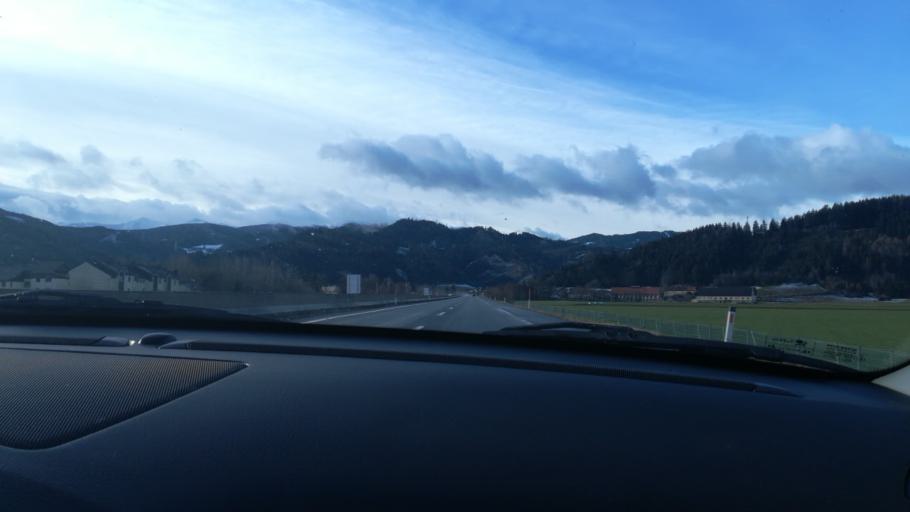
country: AT
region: Styria
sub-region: Politischer Bezirk Murtal
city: Judenburg
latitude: 47.1804
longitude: 14.6657
